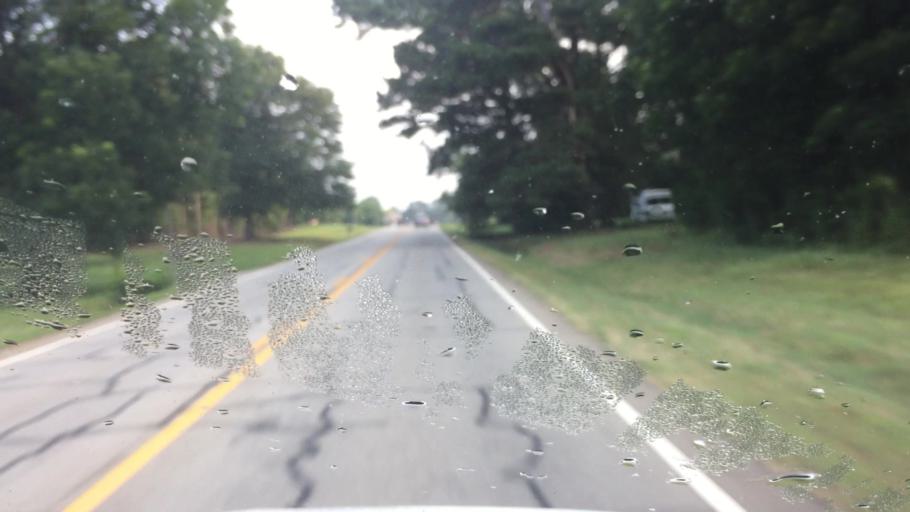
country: US
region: Georgia
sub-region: Henry County
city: Stockbridge
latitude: 33.5802
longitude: -84.1485
